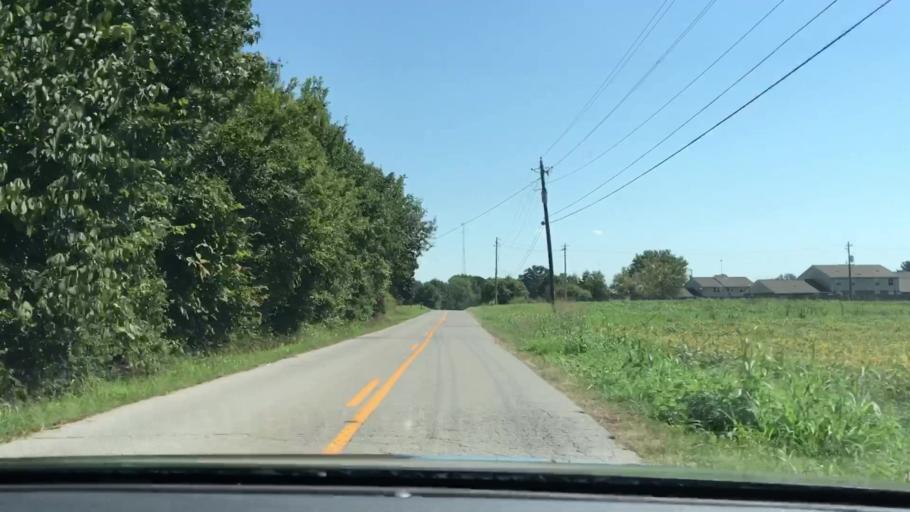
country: US
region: Kentucky
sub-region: Fulton County
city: Fulton
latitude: 36.5214
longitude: -88.8936
